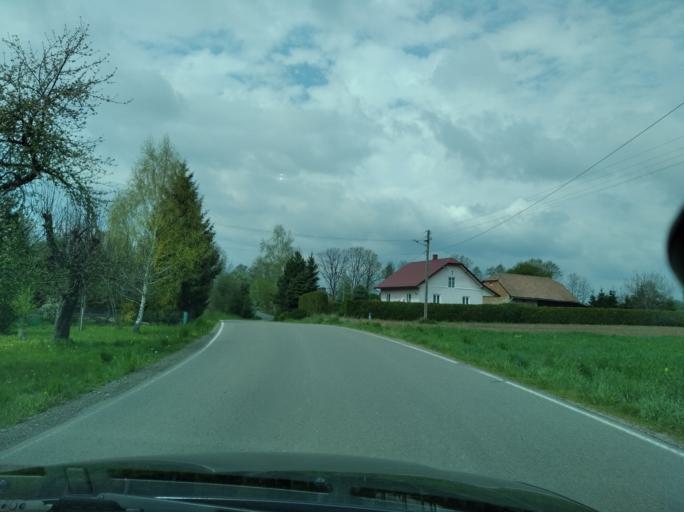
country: PL
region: Subcarpathian Voivodeship
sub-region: Powiat brzozowski
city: Haczow
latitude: 49.6469
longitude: 21.9184
